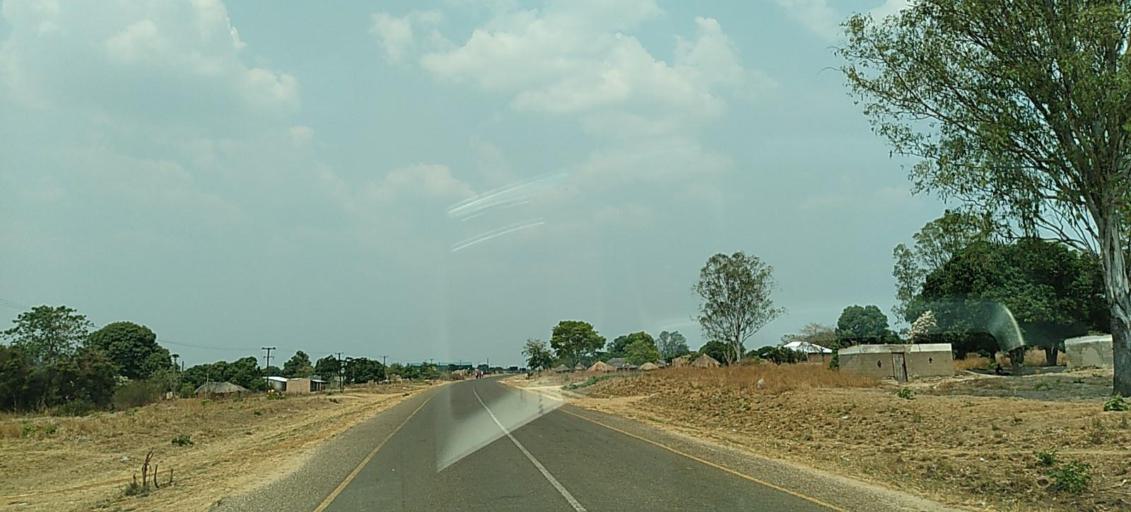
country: ZM
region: North-Western
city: Zambezi
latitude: -13.5505
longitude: 23.1167
